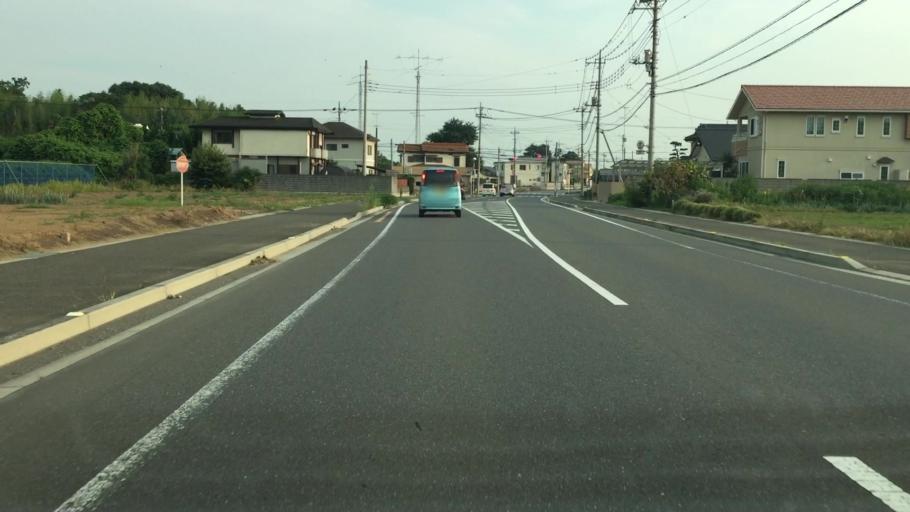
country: JP
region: Gunma
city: Tatebayashi
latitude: 36.2255
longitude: 139.5881
